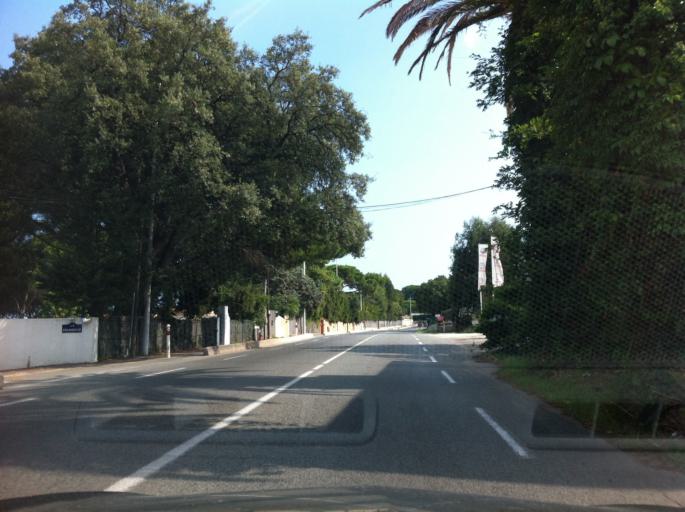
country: FR
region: Provence-Alpes-Cote d'Azur
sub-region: Departement du Var
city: Gassin
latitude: 43.2625
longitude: 6.5998
